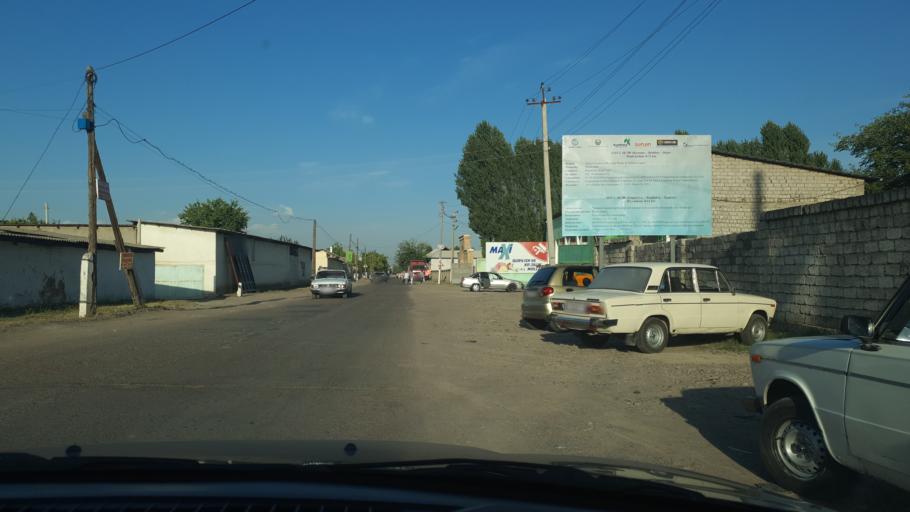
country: UZ
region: Toshkent
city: Tuytepa
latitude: 41.0846
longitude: 69.3275
